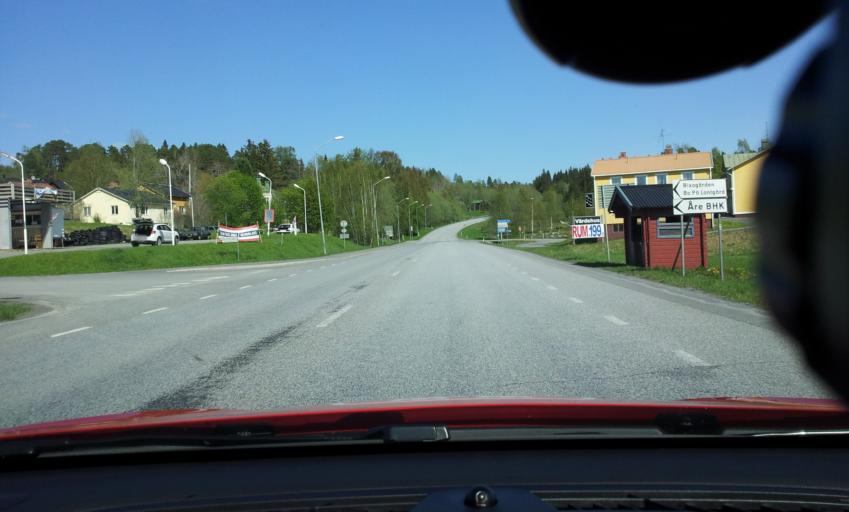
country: SE
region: Jaemtland
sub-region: Are Kommun
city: Jarpen
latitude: 63.3101
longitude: 13.6447
